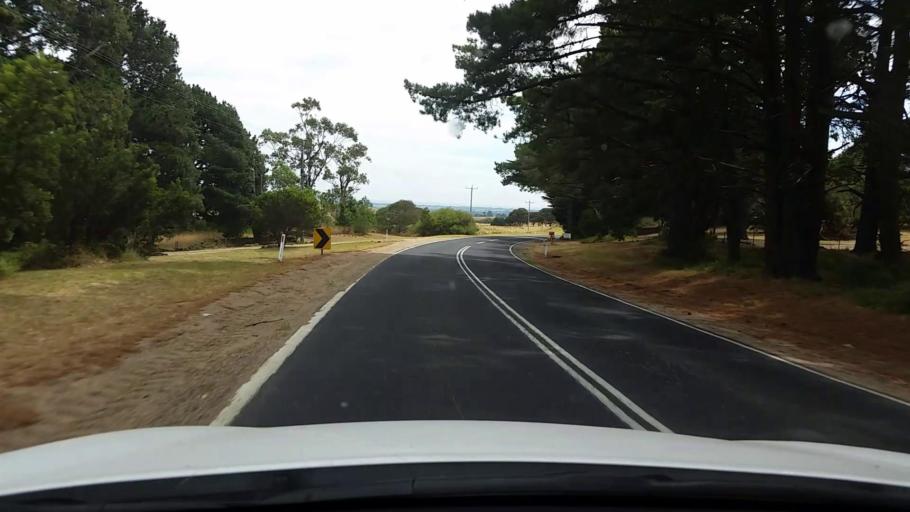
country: AU
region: Victoria
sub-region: Mornington Peninsula
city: Saint Andrews Beach
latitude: -38.4509
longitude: 144.8968
